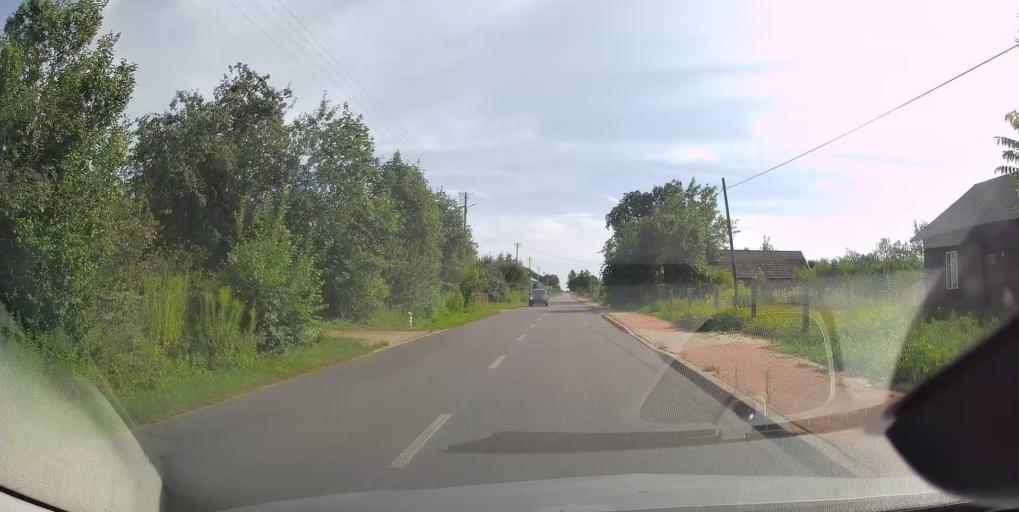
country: PL
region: Lodz Voivodeship
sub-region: Powiat opoczynski
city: Mniszkow
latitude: 51.4250
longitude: 20.0253
